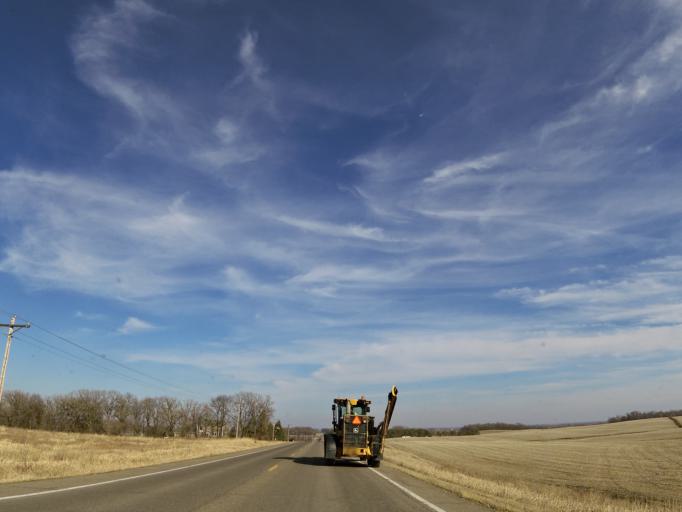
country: US
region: Minnesota
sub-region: Rice County
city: Northfield
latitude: 44.5439
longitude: -93.2203
